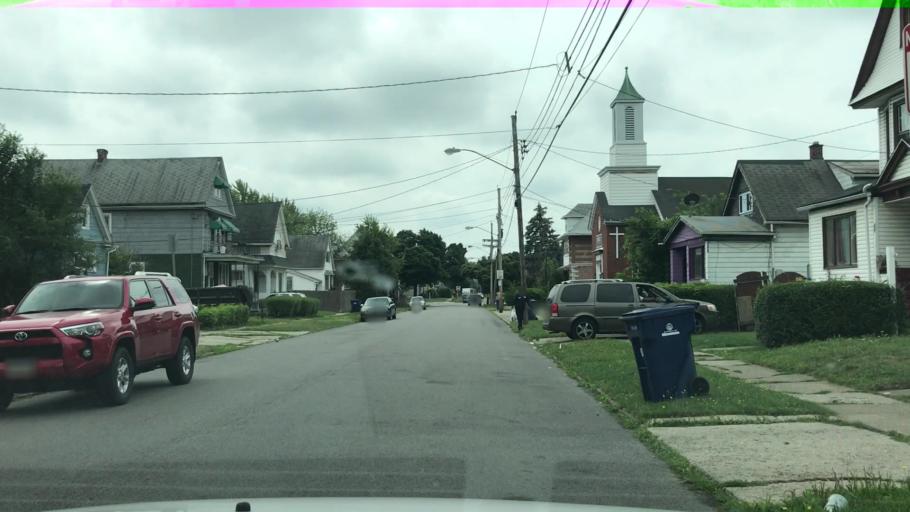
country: US
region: New York
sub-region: Erie County
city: Sloan
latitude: 42.9241
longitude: -78.8022
